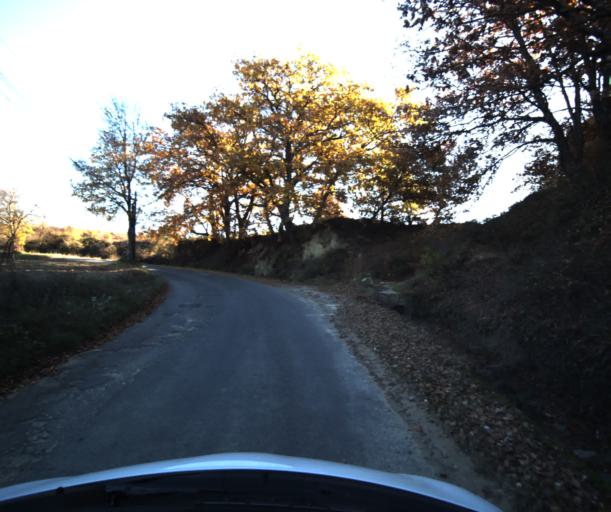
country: FR
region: Provence-Alpes-Cote d'Azur
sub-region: Departement du Vaucluse
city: Pertuis
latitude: 43.7004
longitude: 5.5256
